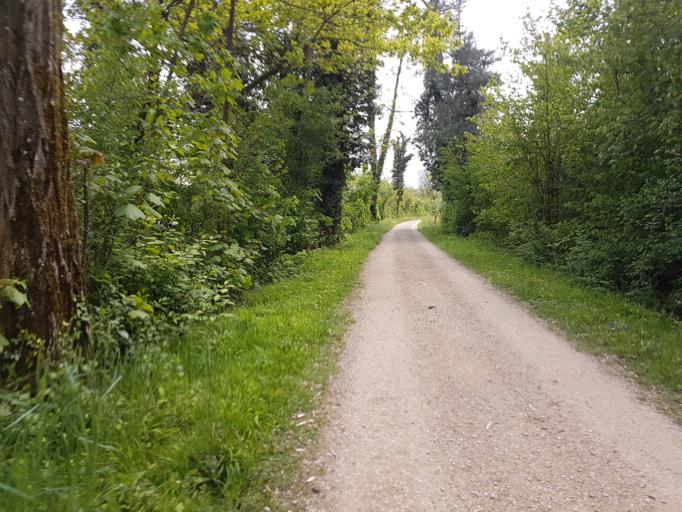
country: CH
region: Aargau
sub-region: Bezirk Brugg
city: Veltheim
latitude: 47.4209
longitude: 8.1619
